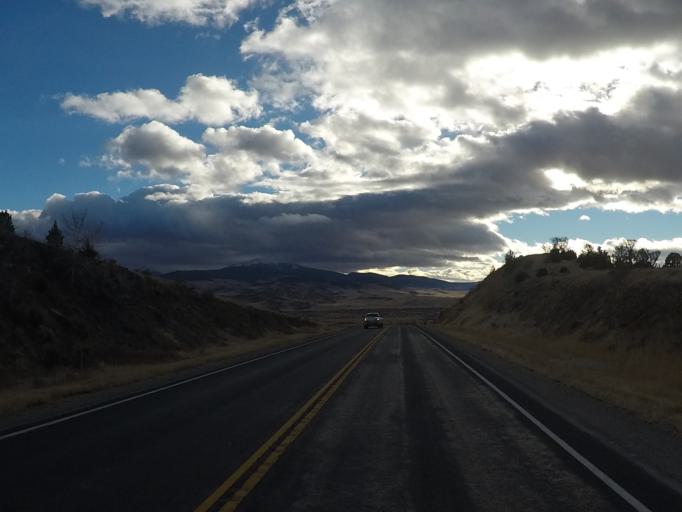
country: US
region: Montana
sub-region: Jefferson County
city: Whitehall
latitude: 45.8896
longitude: -111.9664
